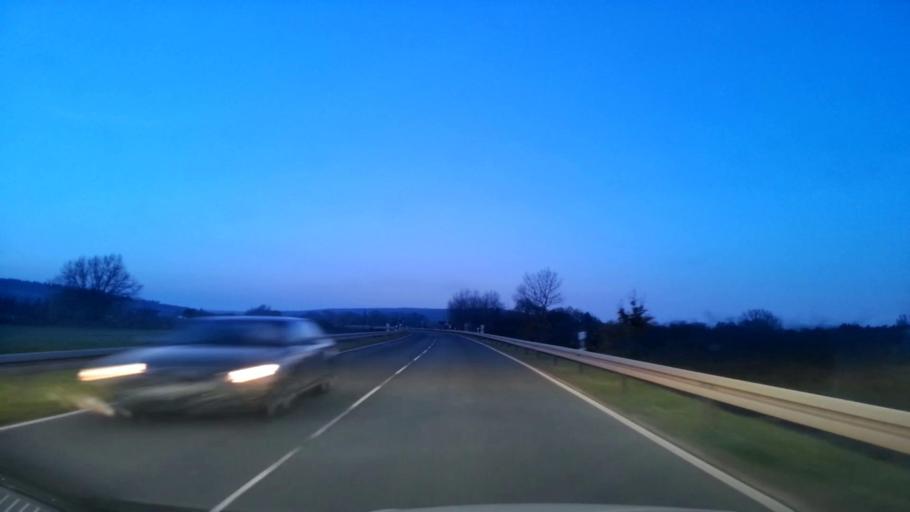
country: DE
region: Bavaria
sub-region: Upper Franconia
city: Pettstadt
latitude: 49.8316
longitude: 10.9400
